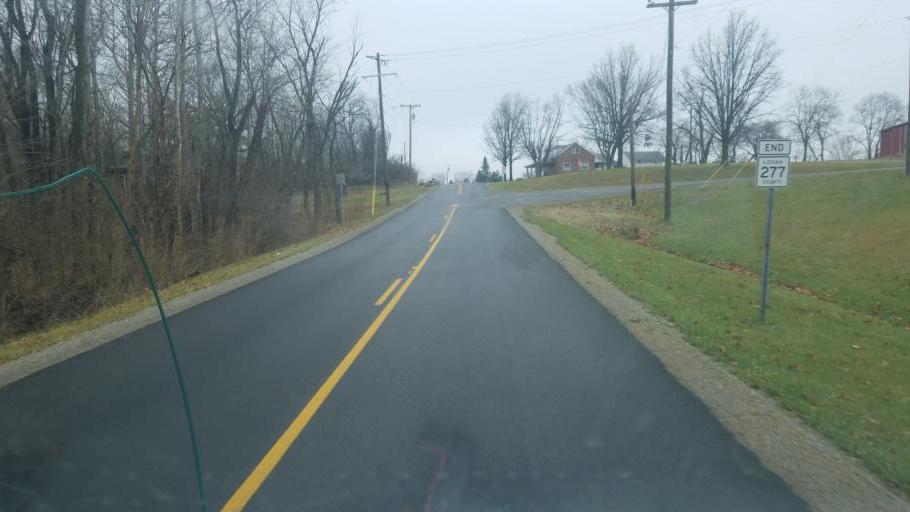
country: US
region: Ohio
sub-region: Champaign County
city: North Lewisburg
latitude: 40.2687
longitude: -83.5577
